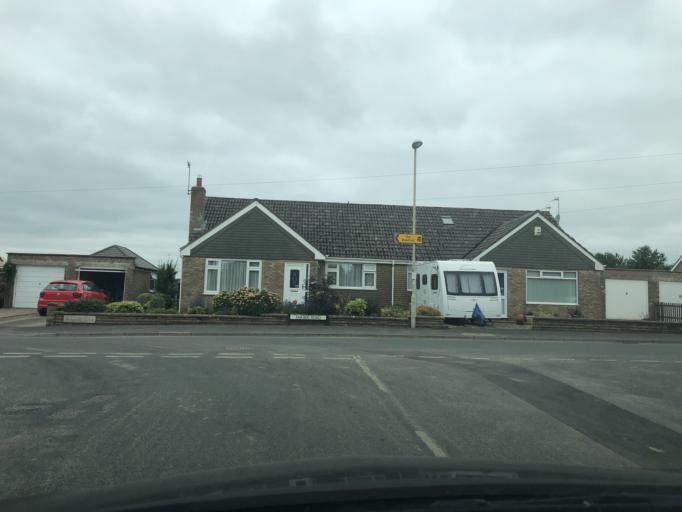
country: GB
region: England
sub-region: North Yorkshire
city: East Ayton
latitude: 54.2440
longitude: -0.4882
